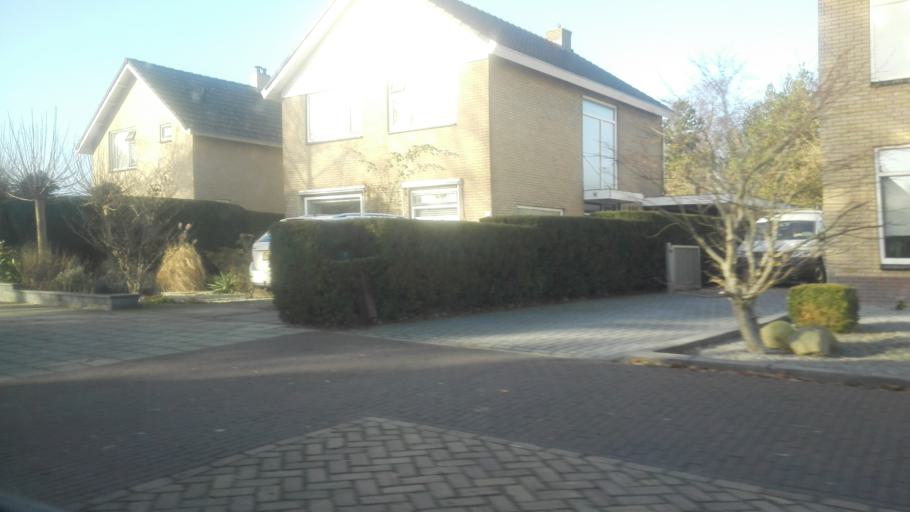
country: NL
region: Friesland
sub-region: Gemeente Heerenveen
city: De Knipe
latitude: 52.9360
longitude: 6.0024
